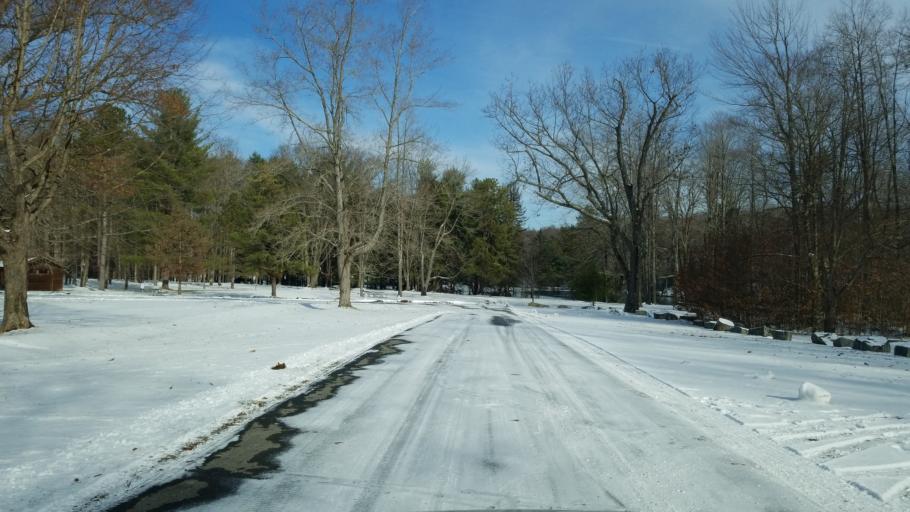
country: US
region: Pennsylvania
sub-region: Clearfield County
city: Clearfield
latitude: 41.1939
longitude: -78.5101
